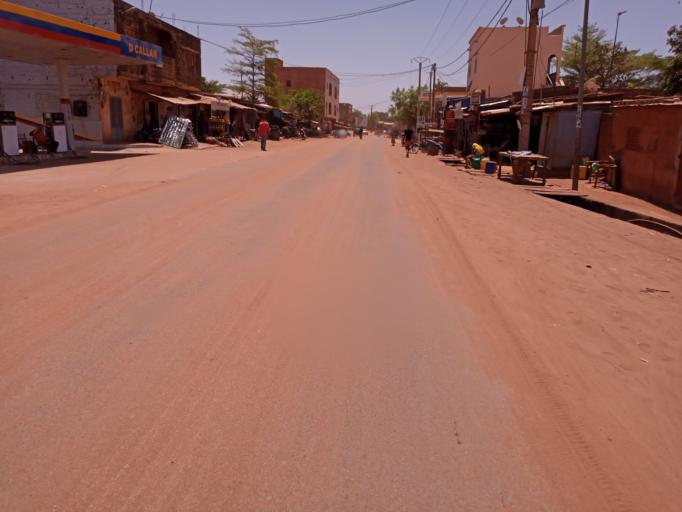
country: ML
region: Bamako
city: Bamako
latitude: 12.5798
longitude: -7.9719
